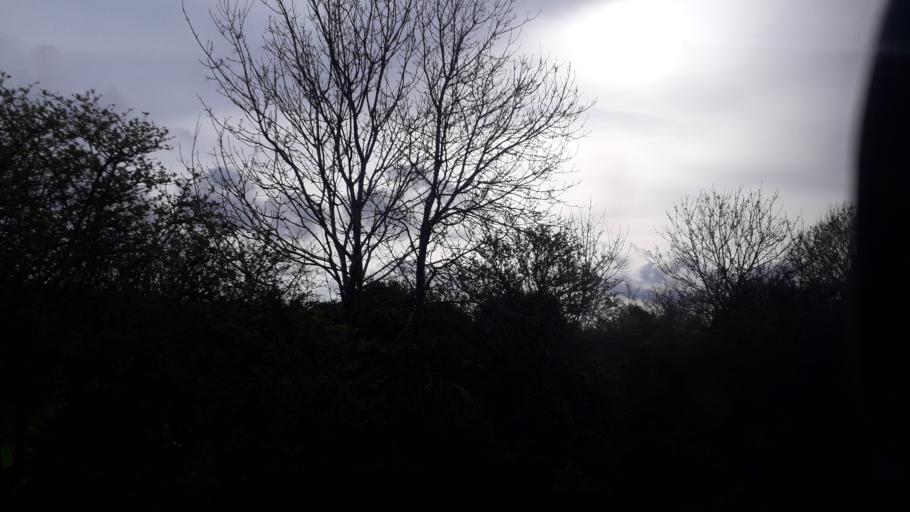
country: IE
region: Leinster
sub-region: An Mhi
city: Enfield
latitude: 53.4134
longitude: -6.8602
